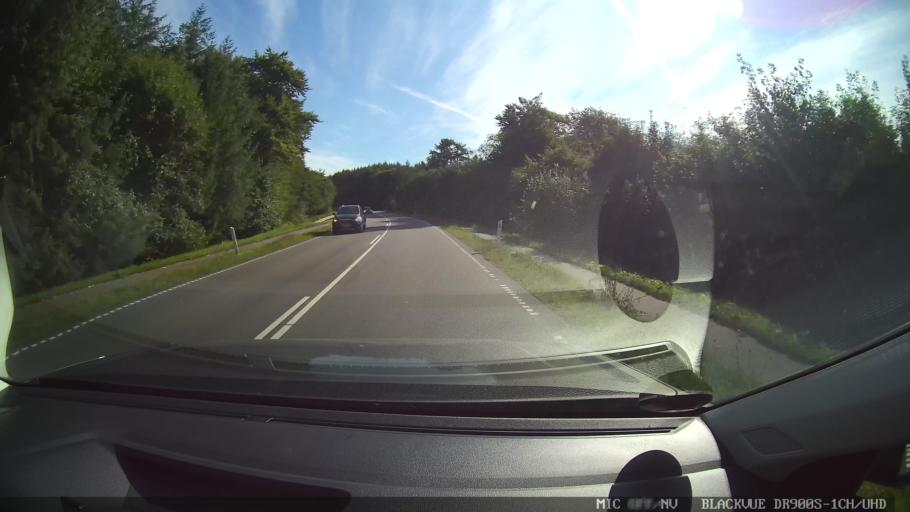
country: DK
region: North Denmark
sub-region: Mariagerfjord Kommune
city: Arden
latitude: 56.7737
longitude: 9.7894
